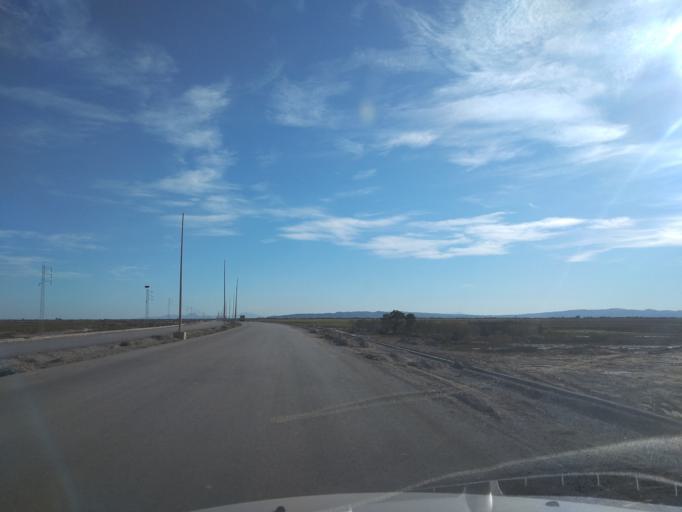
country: TN
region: Ariana
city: Qal'at al Andalus
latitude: 37.0377
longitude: 10.1327
